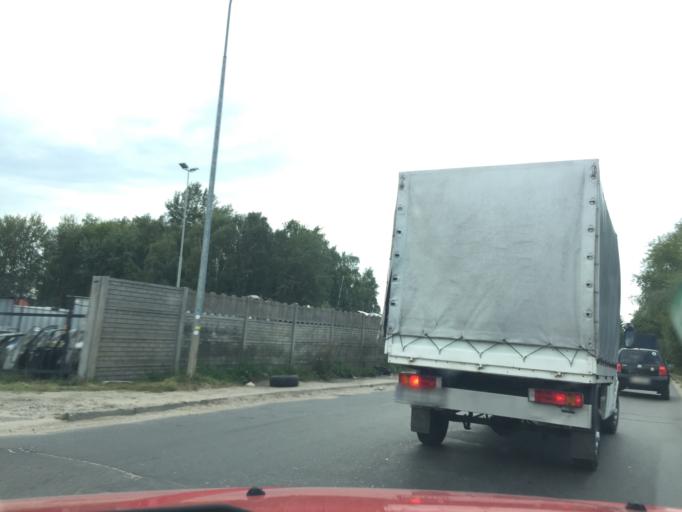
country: PL
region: Greater Poland Voivodeship
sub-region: Powiat poznanski
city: Baranowo
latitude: 52.4203
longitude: 16.8000
